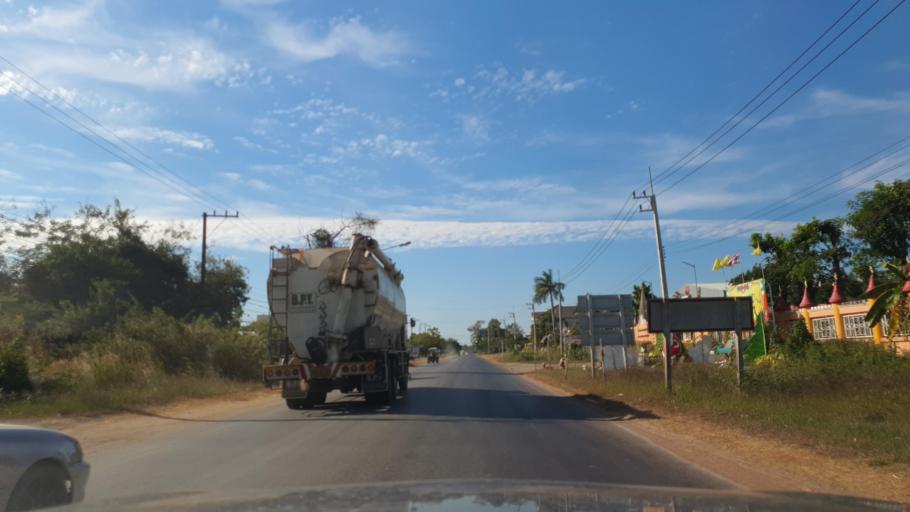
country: TH
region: Kalasin
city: Kuchinarai
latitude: 16.5341
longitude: 104.0725
